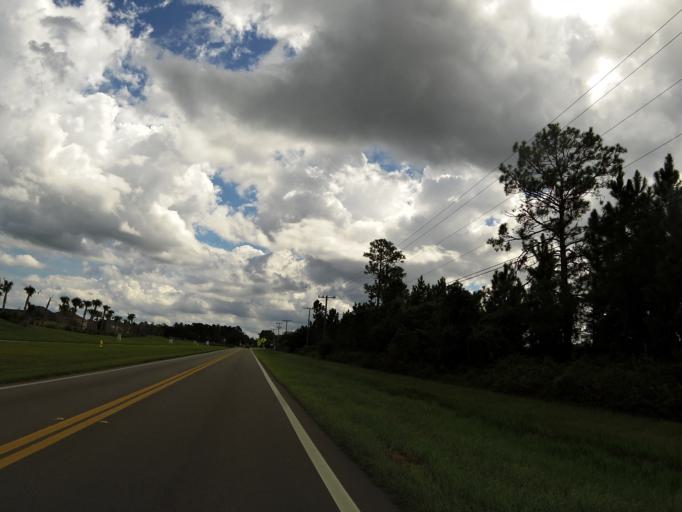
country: US
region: Florida
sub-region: Saint Johns County
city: Saint Augustine
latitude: 29.9249
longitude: -81.4962
